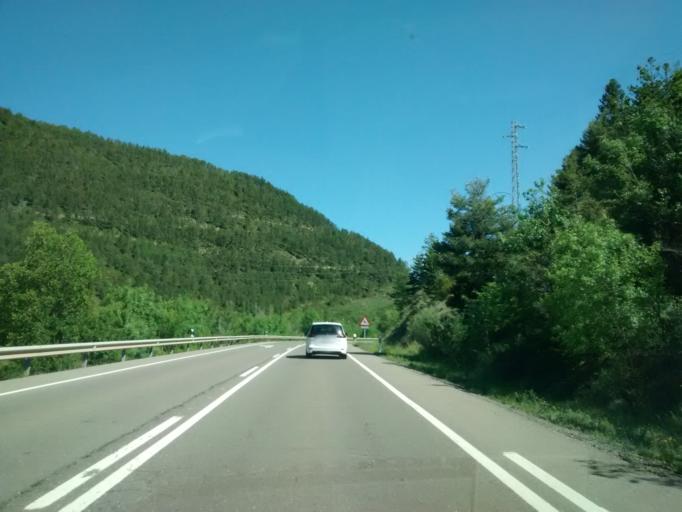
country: ES
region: Aragon
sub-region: Provincia de Huesca
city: Jaca
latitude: 42.5866
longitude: -0.5443
